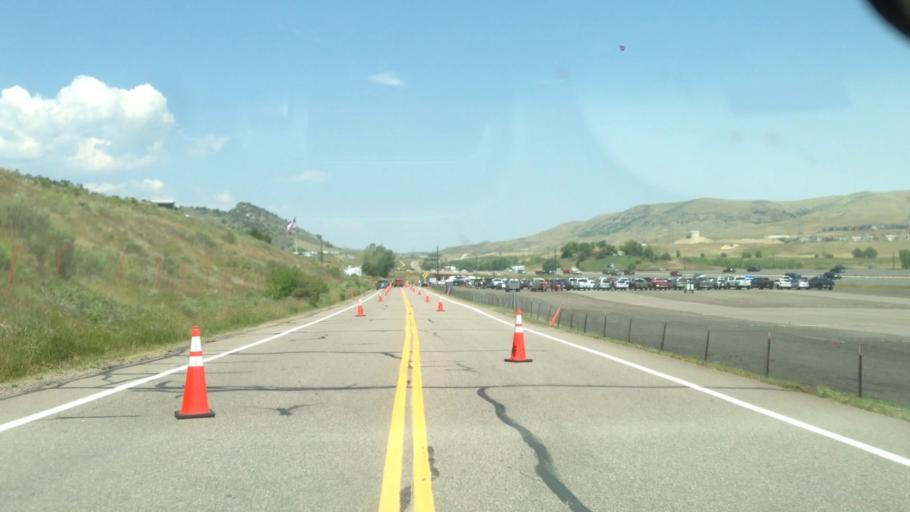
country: US
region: Colorado
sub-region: Jefferson County
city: Indian Hills
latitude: 39.6575
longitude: -105.1837
